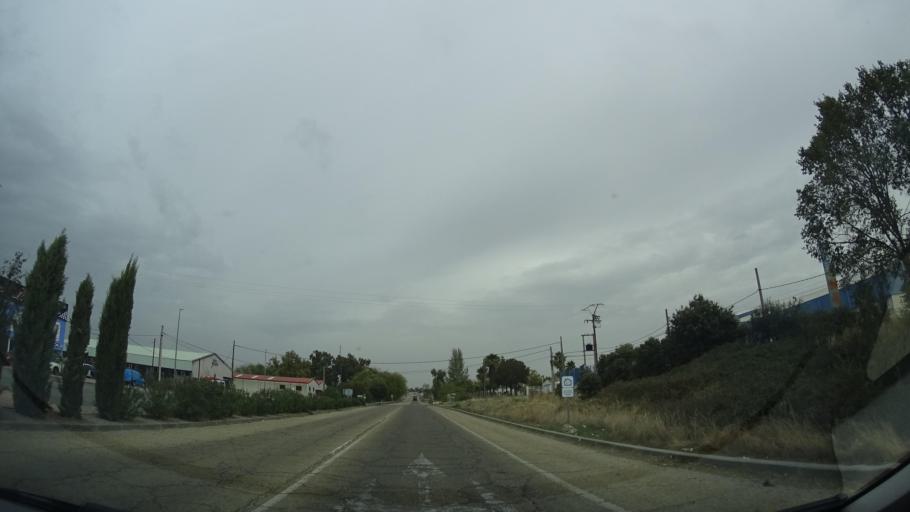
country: ES
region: Extremadura
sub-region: Provincia de Caceres
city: Trujillo
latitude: 39.4784
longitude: -5.8561
